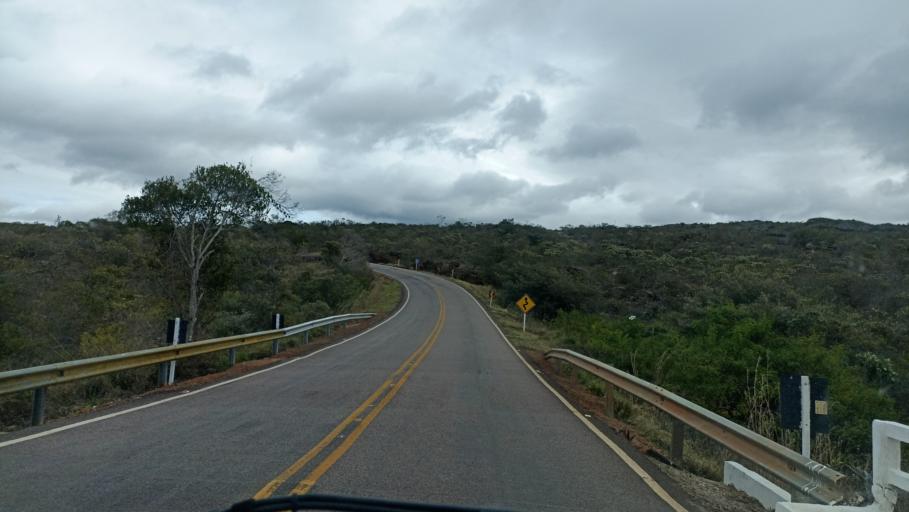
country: BR
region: Bahia
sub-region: Andarai
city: Vera Cruz
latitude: -12.9912
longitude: -41.3505
